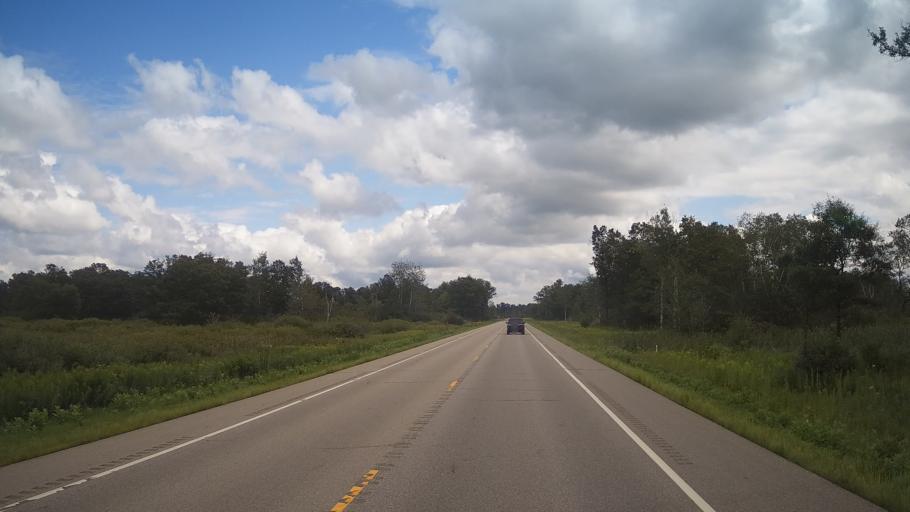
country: US
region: Wisconsin
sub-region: Adams County
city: Friendship
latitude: 44.0257
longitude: -89.6962
